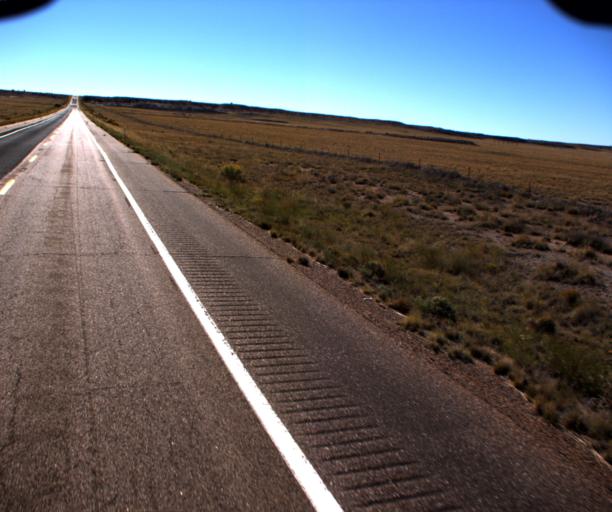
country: US
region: Arizona
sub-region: Navajo County
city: Snowflake
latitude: 34.7259
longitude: -109.7777
